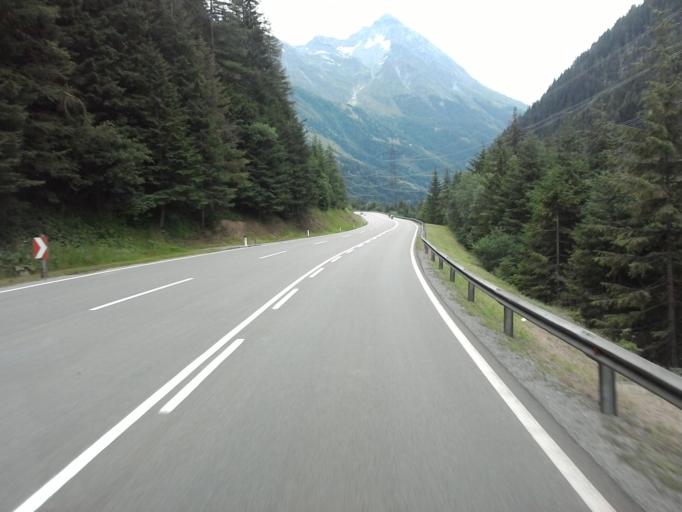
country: AT
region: Tyrol
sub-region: Politischer Bezirk Lienz
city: Matrei in Osttirol
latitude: 47.0961
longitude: 12.5181
